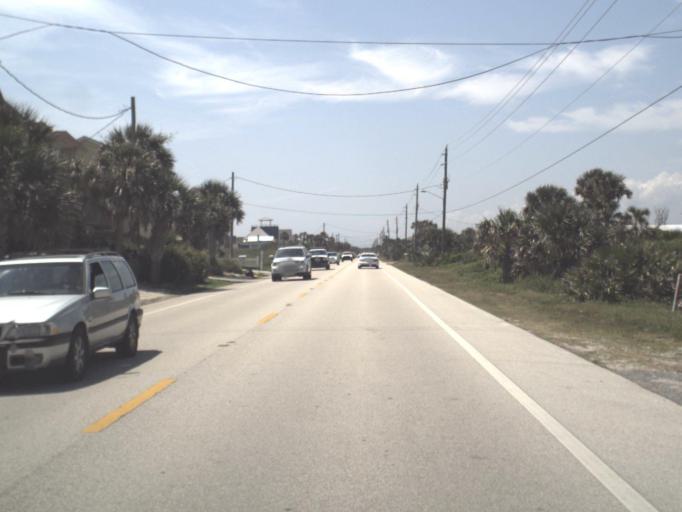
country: US
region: Florida
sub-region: Saint Johns County
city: Villano Beach
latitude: 29.9302
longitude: -81.2969
